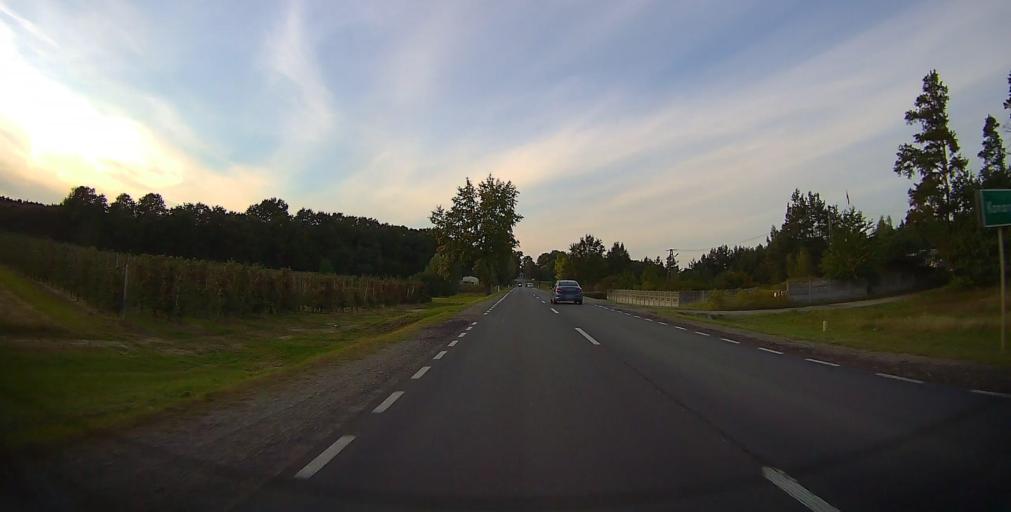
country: PL
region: Masovian Voivodeship
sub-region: Powiat otwocki
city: Sobienie Jeziory
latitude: 51.8725
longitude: 21.2404
